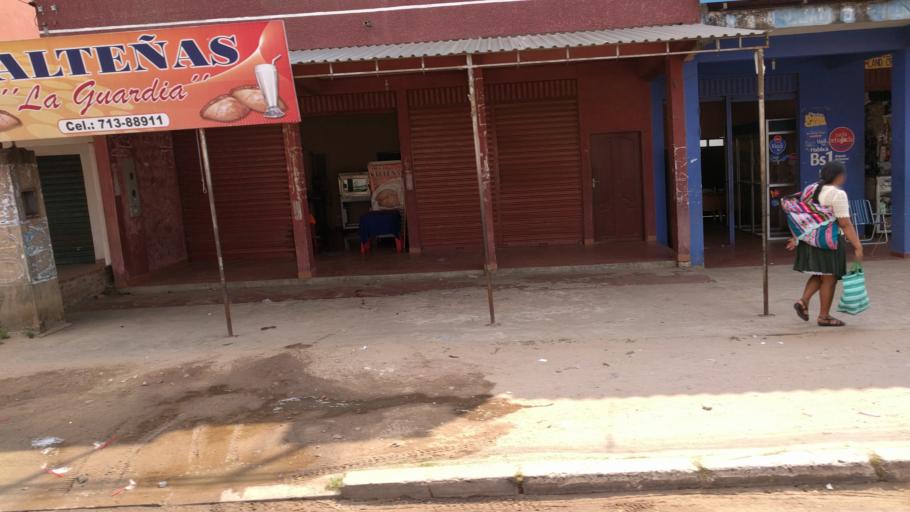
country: BO
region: Santa Cruz
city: Santiago del Torno
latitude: -17.9979
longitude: -63.3858
